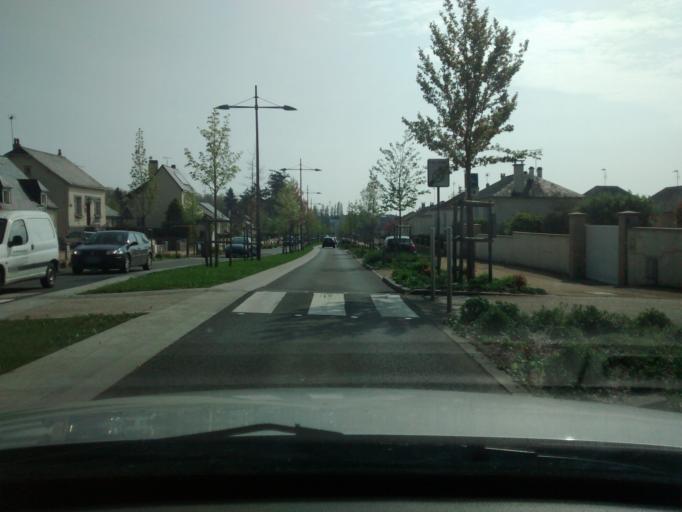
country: FR
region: Pays de la Loire
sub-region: Departement de la Mayenne
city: Saint-Berthevin
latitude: 48.0689
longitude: -0.8231
